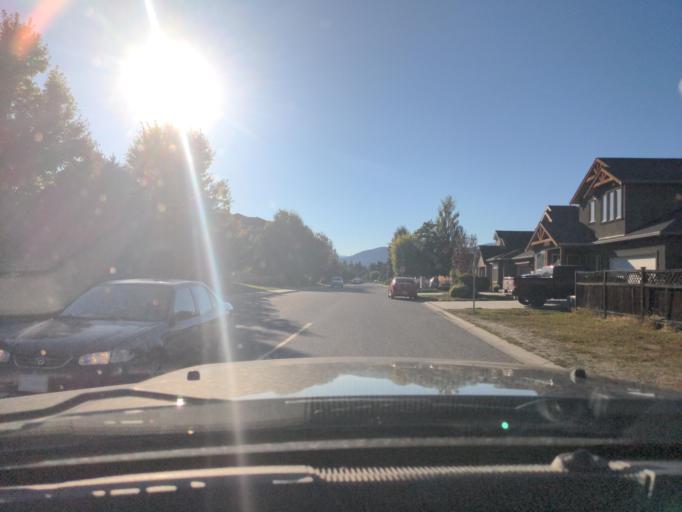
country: CA
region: British Columbia
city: Kelowna
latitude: 49.8539
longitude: -119.4748
